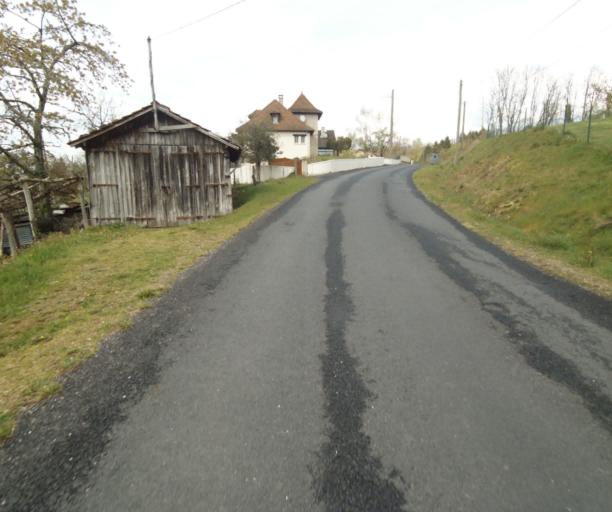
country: FR
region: Limousin
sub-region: Departement de la Correze
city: Tulle
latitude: 45.2675
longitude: 1.7501
